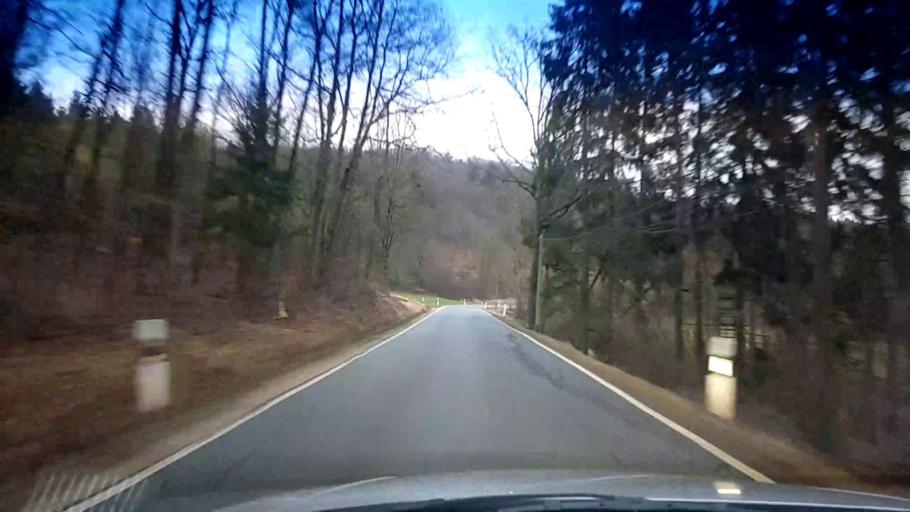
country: DE
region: Bavaria
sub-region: Upper Franconia
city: Wattendorf
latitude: 50.0553
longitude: 11.0593
